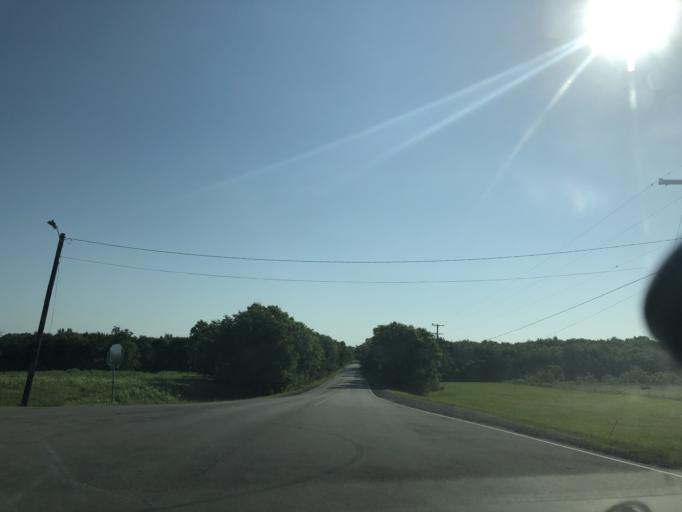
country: US
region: Texas
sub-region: Dallas County
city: Sunnyvale
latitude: 32.8147
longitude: -96.5596
